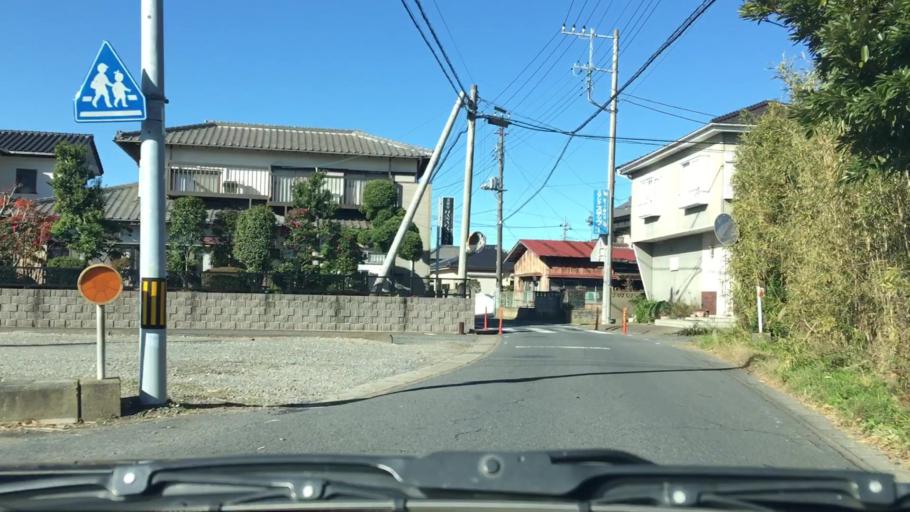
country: JP
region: Chiba
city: Omigawa
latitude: 35.8650
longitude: 140.6655
